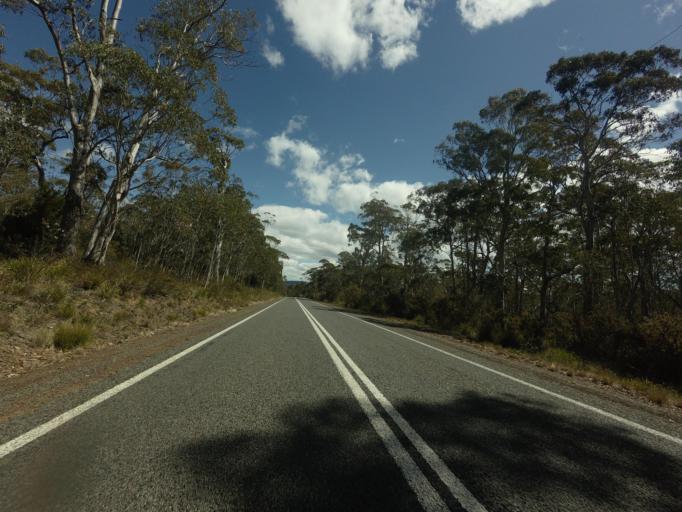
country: AU
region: Tasmania
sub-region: Northern Midlands
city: Evandale
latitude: -42.0273
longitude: 147.8352
